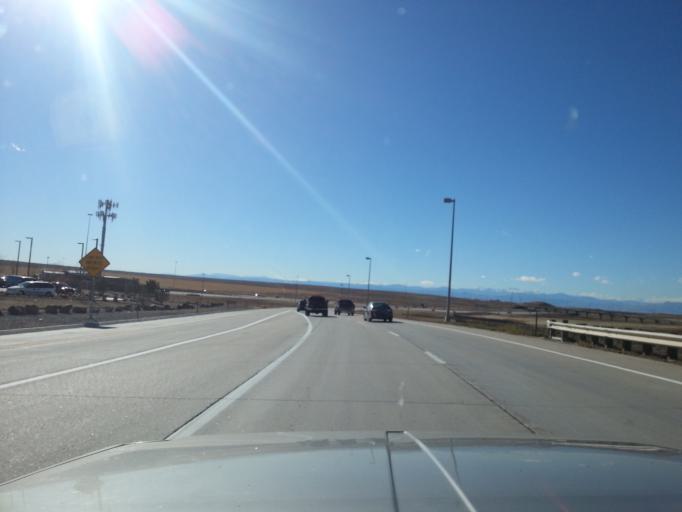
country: US
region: Colorado
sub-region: Adams County
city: Aurora
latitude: 39.8374
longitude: -104.7201
